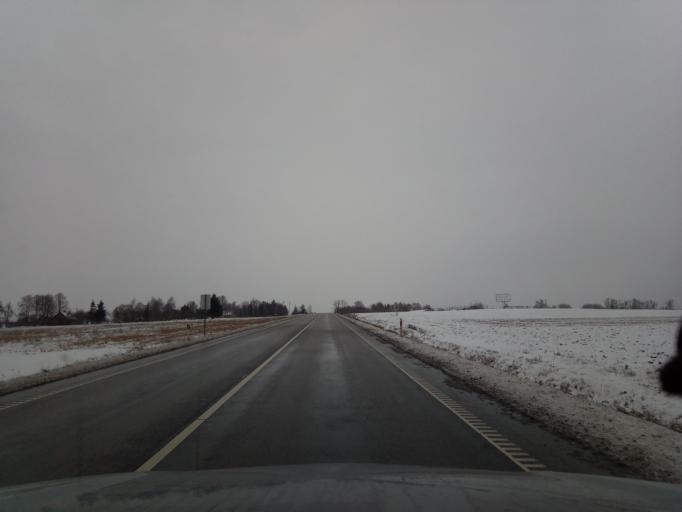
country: LT
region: Panevezys
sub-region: Panevezys City
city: Panevezys
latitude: 55.6236
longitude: 24.3476
